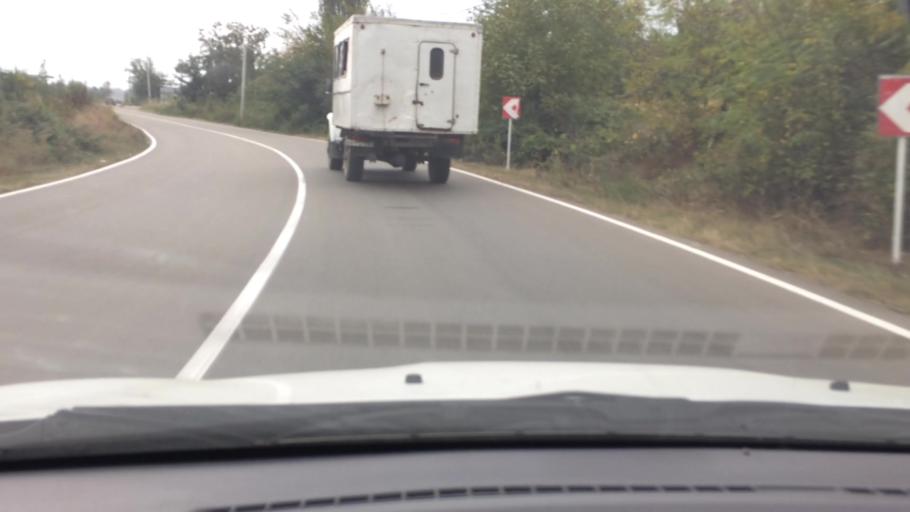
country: AM
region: Tavush
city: Bagratashen
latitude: 41.2659
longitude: 44.7921
